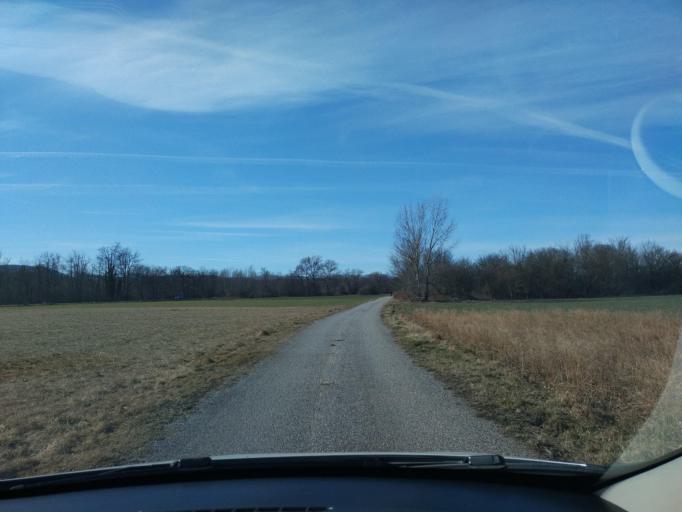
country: AT
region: Lower Austria
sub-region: Politischer Bezirk Neunkirchen
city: Pitten
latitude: 47.7384
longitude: 16.1931
